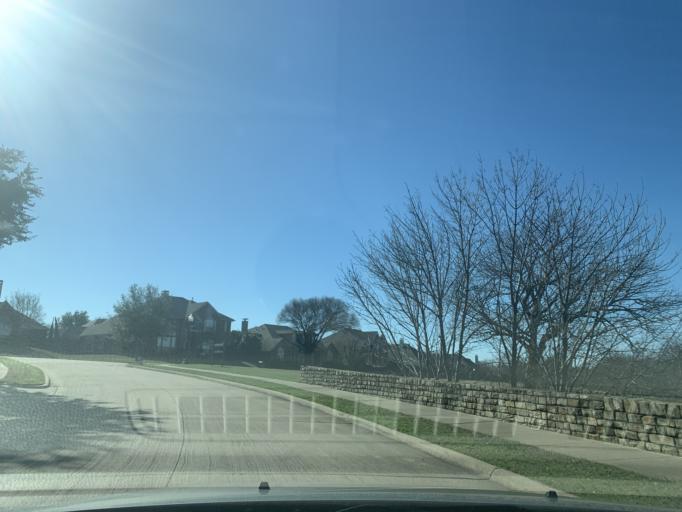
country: US
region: Texas
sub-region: Denton County
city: The Colony
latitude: 33.0650
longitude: -96.8369
